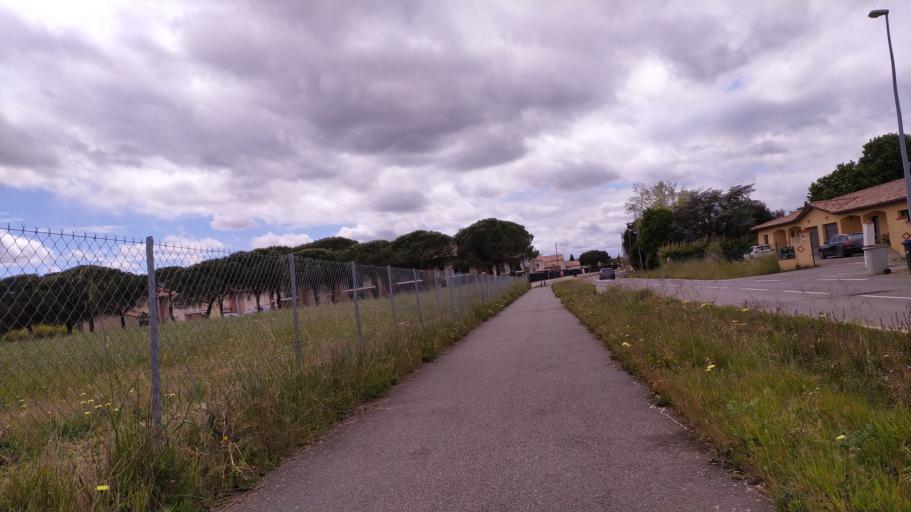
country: FR
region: Midi-Pyrenees
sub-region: Departement de la Haute-Garonne
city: Tournefeuille
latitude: 43.5843
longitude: 1.3092
